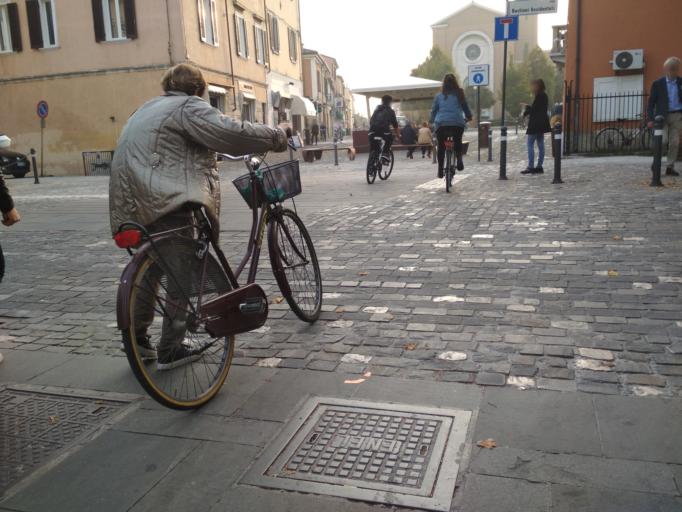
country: IT
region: Emilia-Romagna
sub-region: Provincia di Rimini
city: Rimini
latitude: 44.0574
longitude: 12.5651
